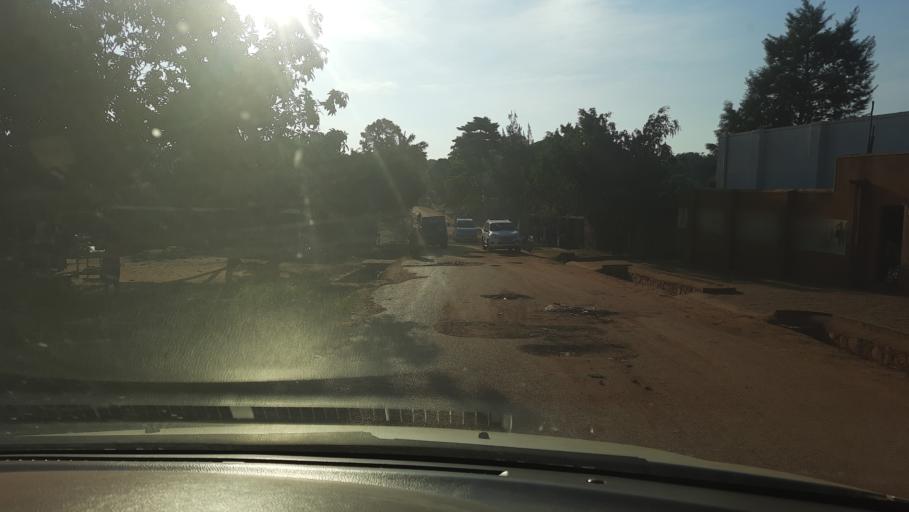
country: UG
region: Central Region
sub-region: Mukono District
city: Mukono
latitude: 0.3709
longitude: 32.7523
